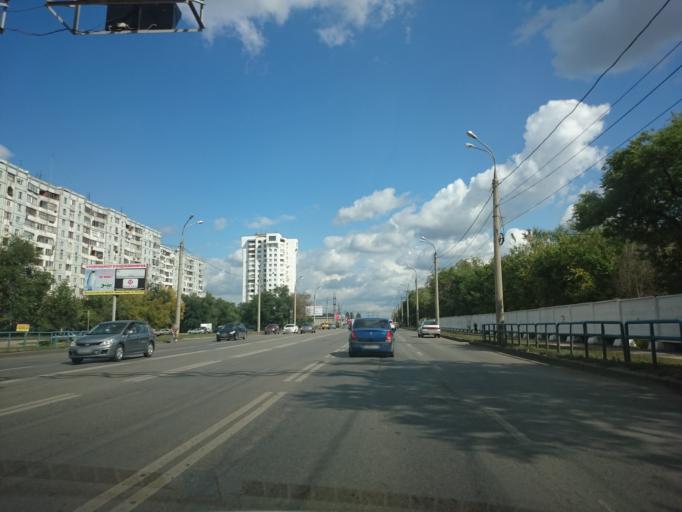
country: RU
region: Samara
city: Samara
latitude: 53.2582
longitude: 50.2345
